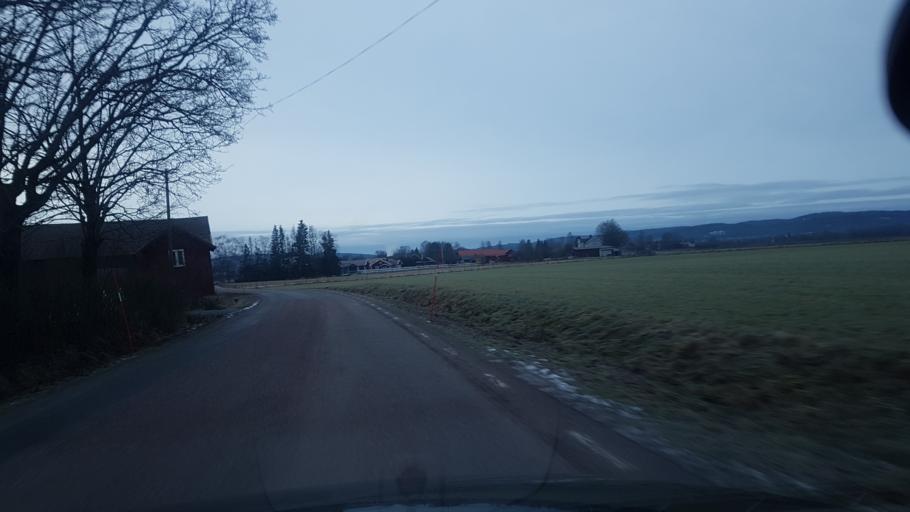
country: SE
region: Dalarna
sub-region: Saters Kommun
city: Saeter
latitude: 60.4281
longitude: 15.6567
